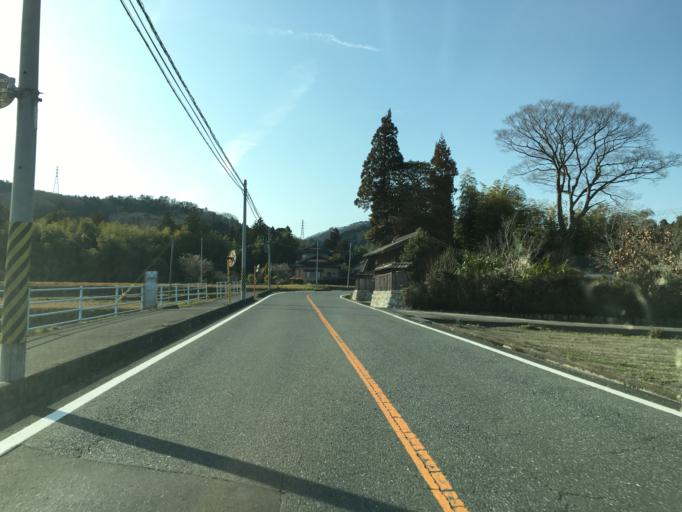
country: JP
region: Ibaraki
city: Takahagi
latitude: 36.7222
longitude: 140.6763
